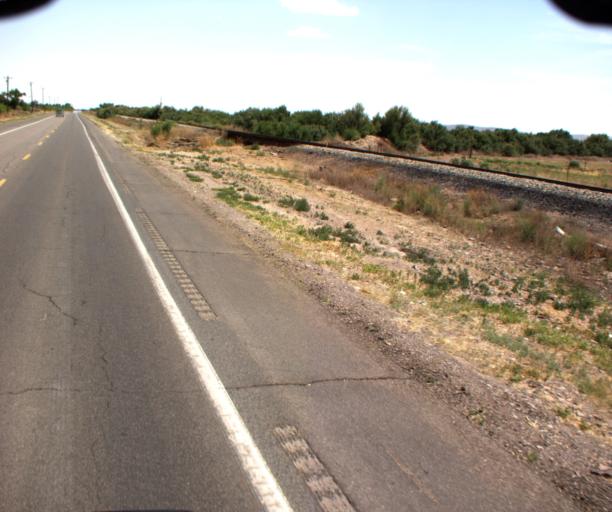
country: US
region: Arizona
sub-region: Greenlee County
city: Clifton
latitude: 32.7034
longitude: -109.0912
